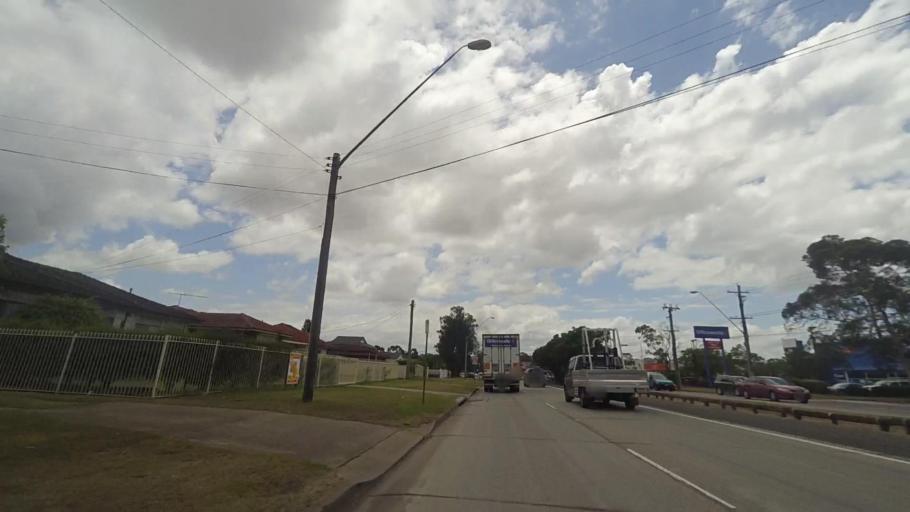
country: AU
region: New South Wales
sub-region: Fairfield
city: Cabramatta West
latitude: -33.9096
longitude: 150.9187
